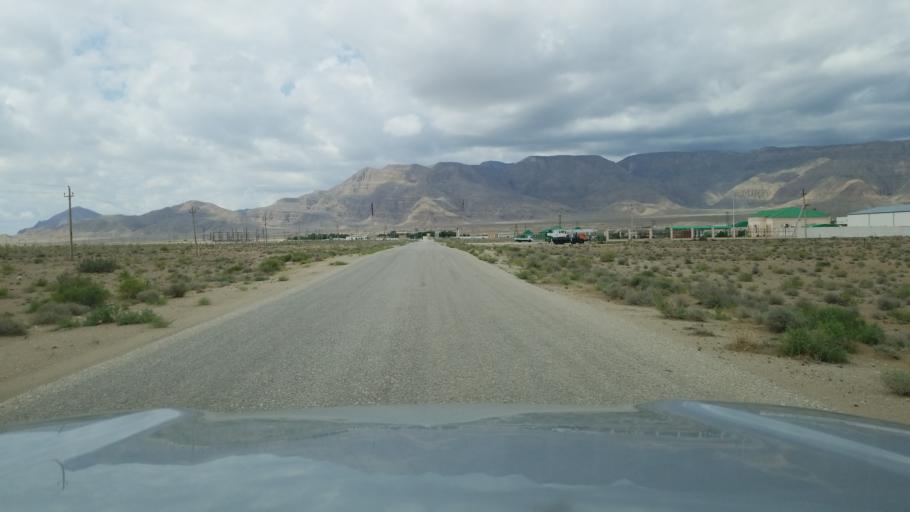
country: TM
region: Balkan
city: Balkanabat
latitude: 39.4728
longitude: 54.4628
